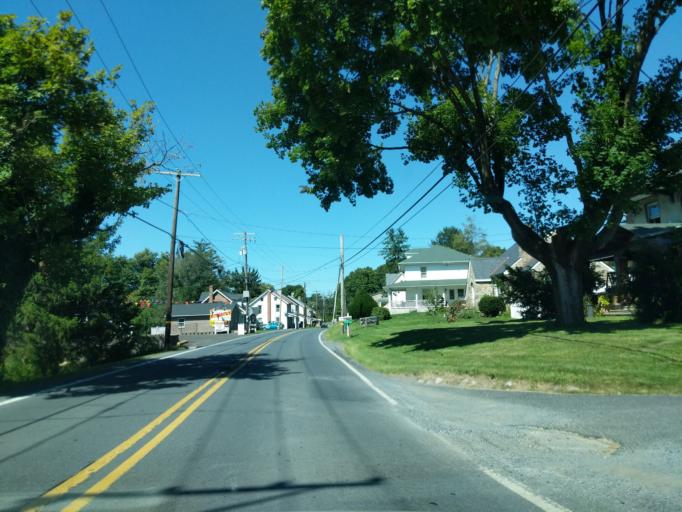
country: US
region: Pennsylvania
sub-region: Lehigh County
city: Coopersburg
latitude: 40.5084
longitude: -75.4471
